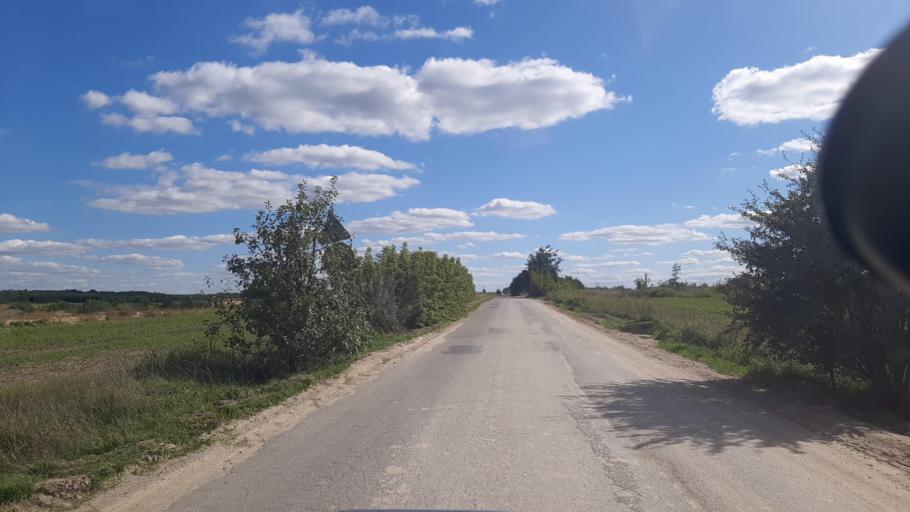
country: PL
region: Lublin Voivodeship
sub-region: Powiat pulawski
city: Markuszow
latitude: 51.4127
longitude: 22.2302
